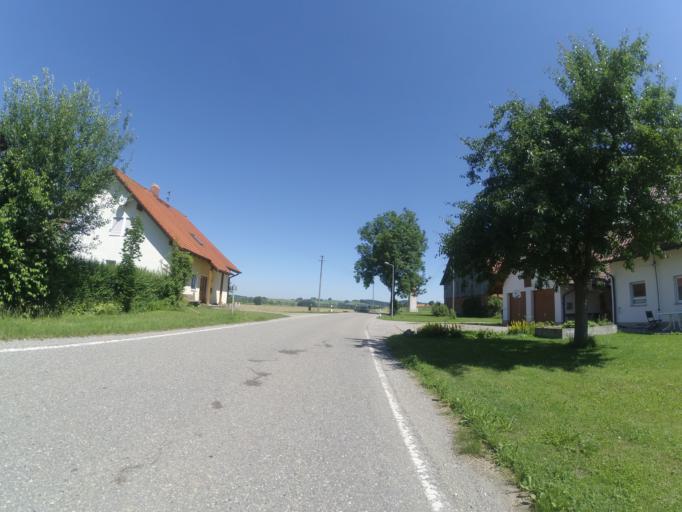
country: DE
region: Baden-Wuerttemberg
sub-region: Tuebingen Region
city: Bad Wurzach
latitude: 47.8678
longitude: 9.9330
